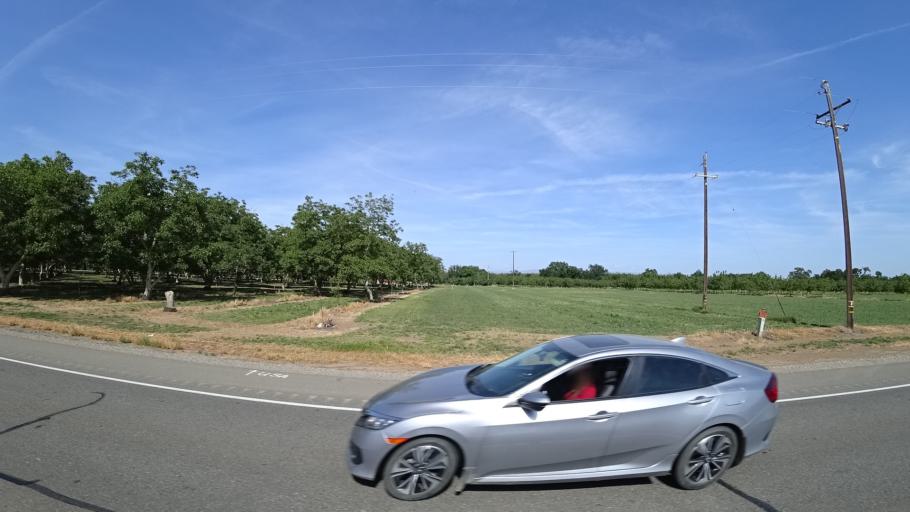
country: US
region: California
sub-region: Tehama County
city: Los Molinos
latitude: 39.9881
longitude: -122.0832
